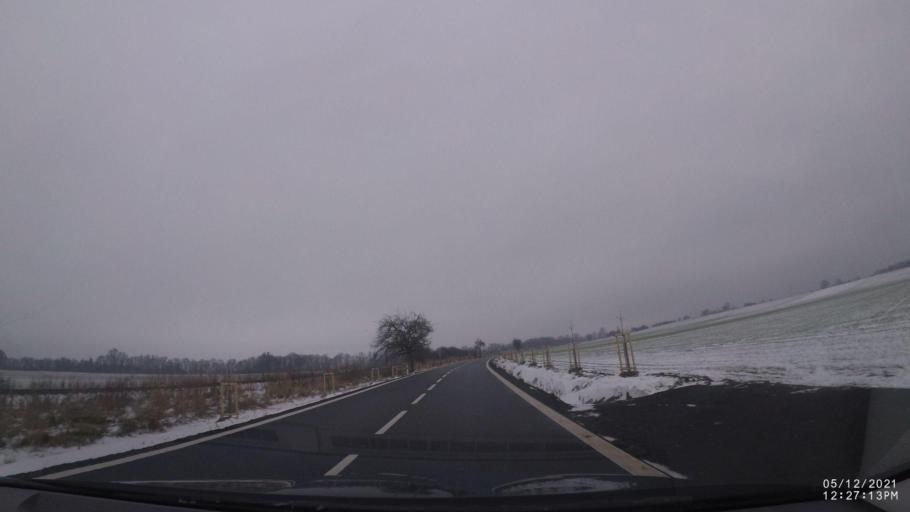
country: CZ
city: Nove Mesto nad Metuji
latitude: 50.3372
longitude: 16.1081
